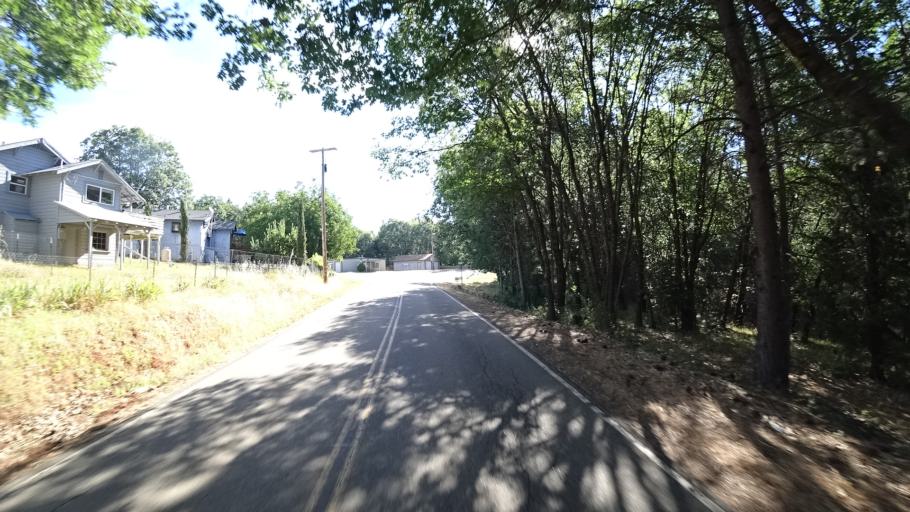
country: US
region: California
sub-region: Amador County
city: Pioneer
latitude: 38.3786
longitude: -120.5147
